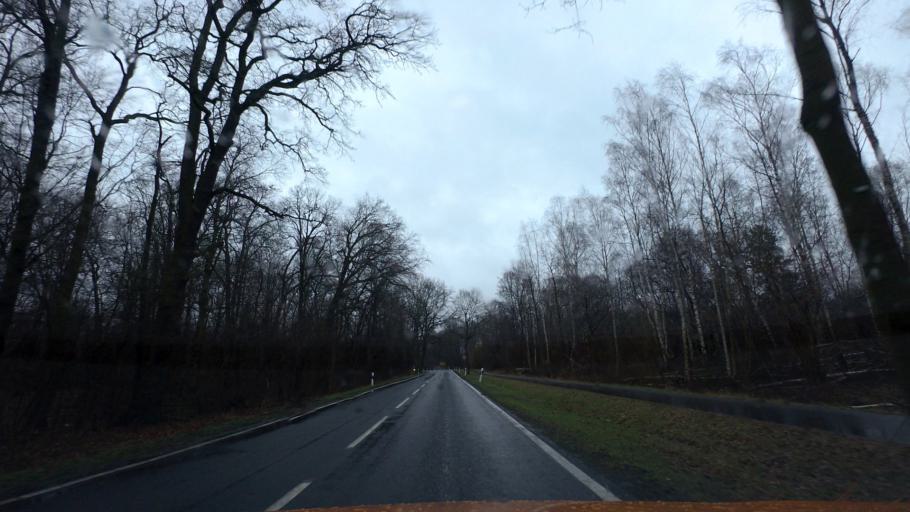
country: DE
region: Brandenburg
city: Brieselang
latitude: 52.5934
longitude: 13.0449
